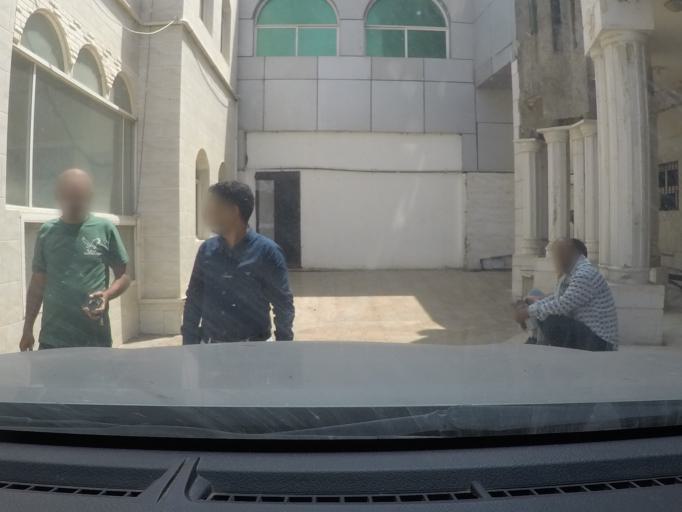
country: YE
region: Aden
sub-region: Khur Maksar
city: Khawr Maksar
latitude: 12.8114
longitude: 45.0424
